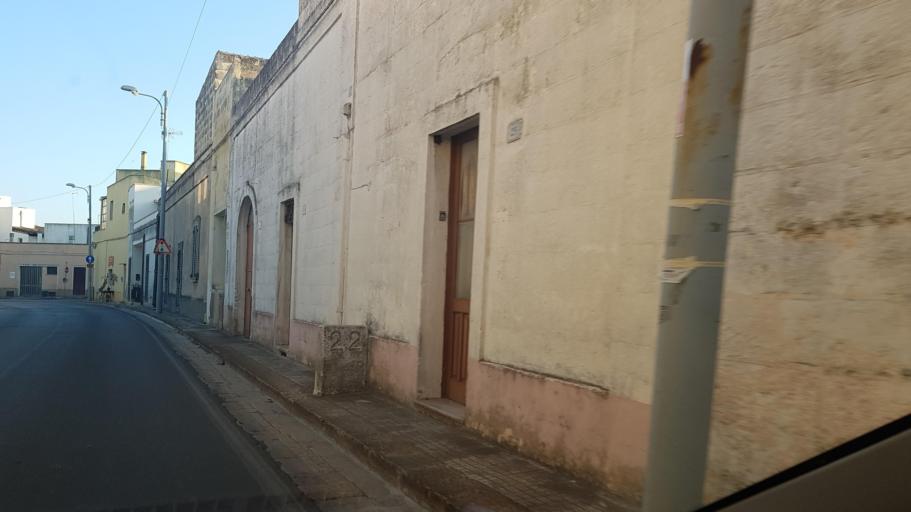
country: IT
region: Apulia
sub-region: Provincia di Lecce
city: Lucugnano
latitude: 39.9355
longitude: 18.3192
